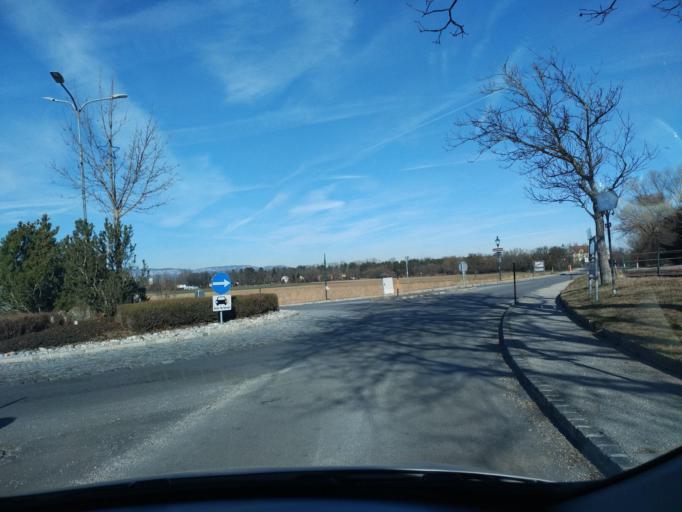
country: AT
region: Lower Austria
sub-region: Politischer Bezirk Wiener Neustadt
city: Lanzenkirchen
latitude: 47.7379
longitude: 16.2503
